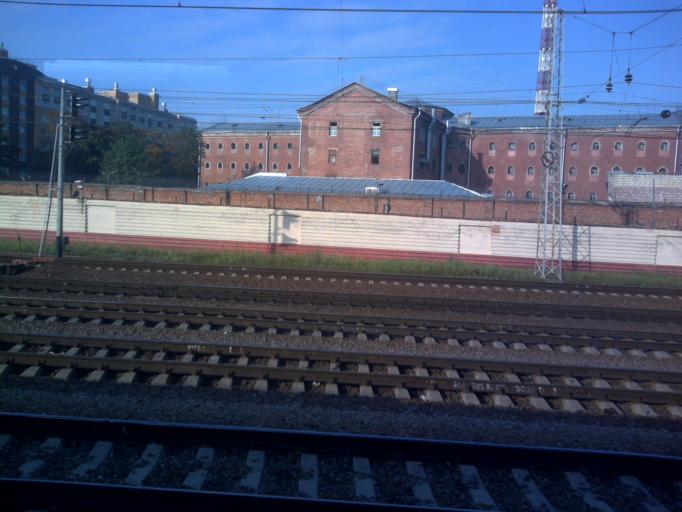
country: RU
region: Leningrad
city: Finlyandskiy
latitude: 59.9628
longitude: 30.3594
